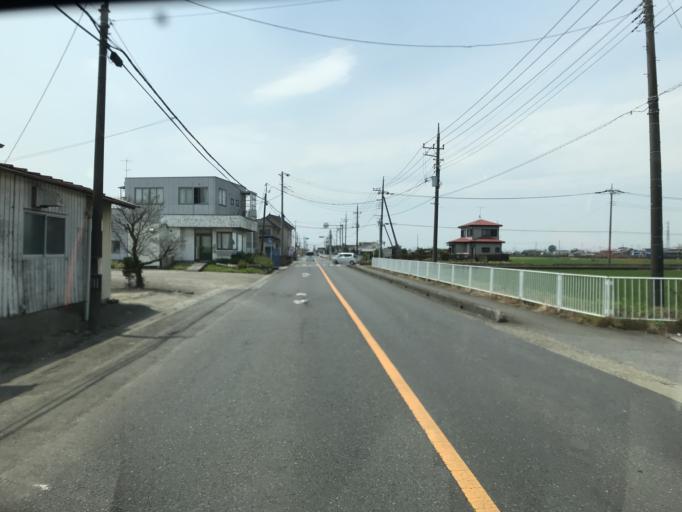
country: JP
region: Saitama
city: Satte
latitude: 36.0759
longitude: 139.7443
